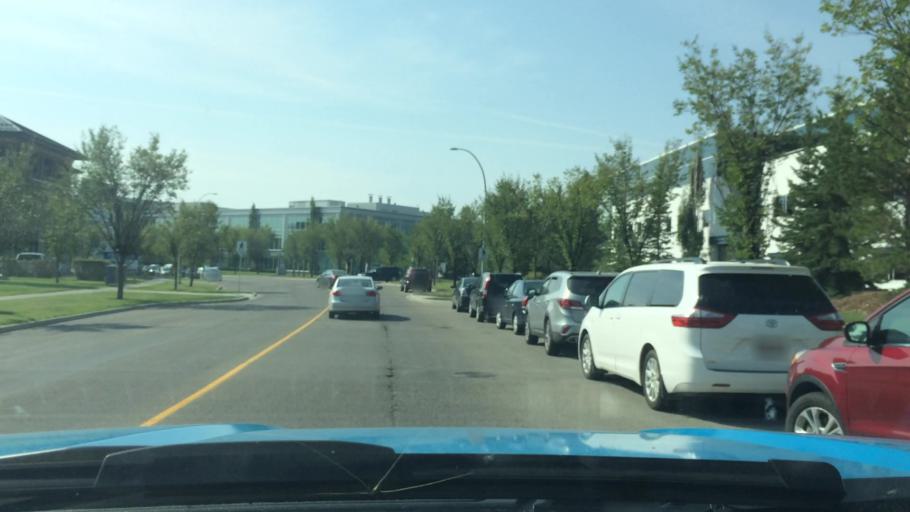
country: CA
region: Alberta
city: Calgary
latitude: 50.9029
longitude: -114.0580
